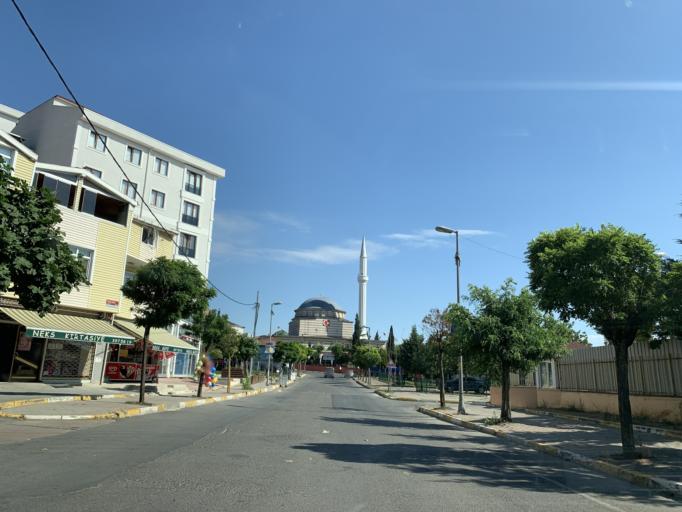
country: TR
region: Istanbul
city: Pendik
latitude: 40.8817
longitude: 29.2803
